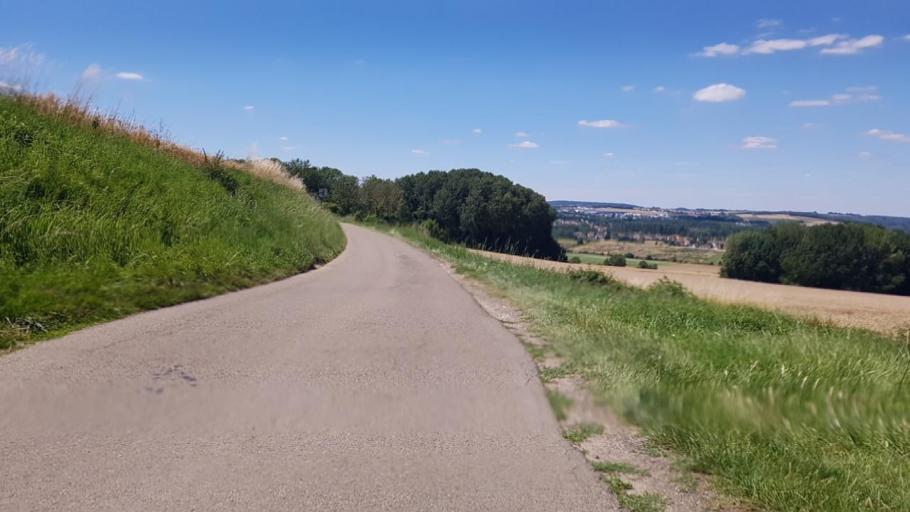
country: FR
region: Ile-de-France
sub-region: Departement de Seine-et-Marne
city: Trilport
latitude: 48.9377
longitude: 2.9572
